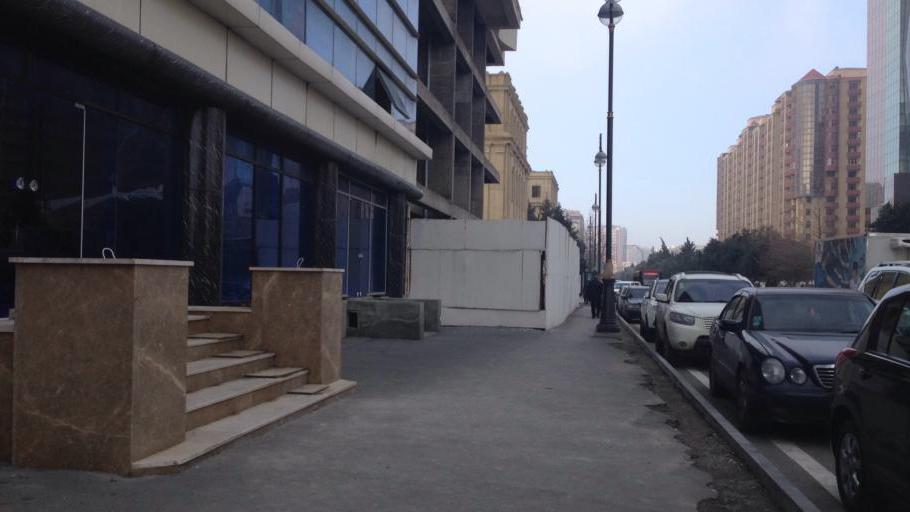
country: AZ
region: Baki
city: Baku
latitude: 40.3828
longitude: 49.8735
